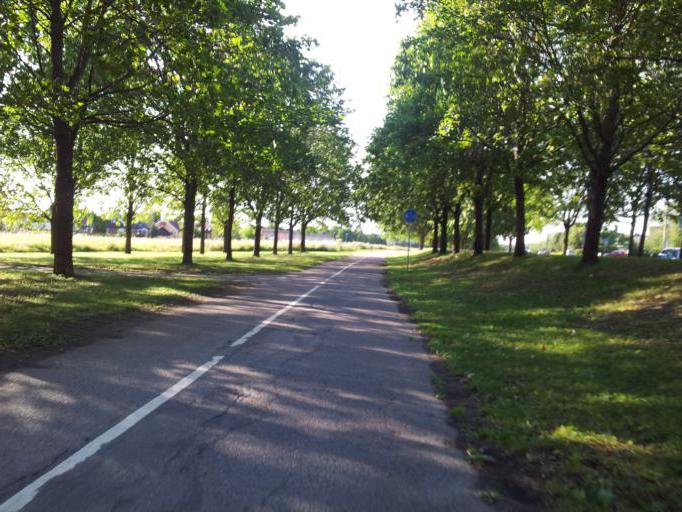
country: SE
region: Uppsala
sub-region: Uppsala Kommun
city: Saevja
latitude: 59.8599
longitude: 17.6858
